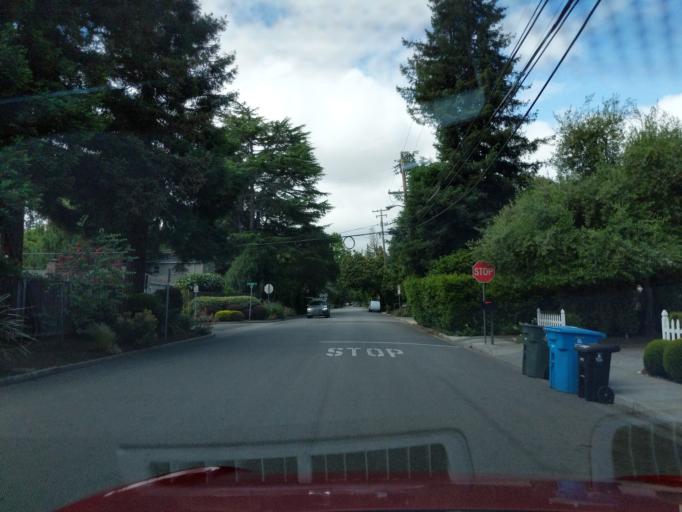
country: US
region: California
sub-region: San Mateo County
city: Menlo Park
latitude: 37.4465
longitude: -122.1757
